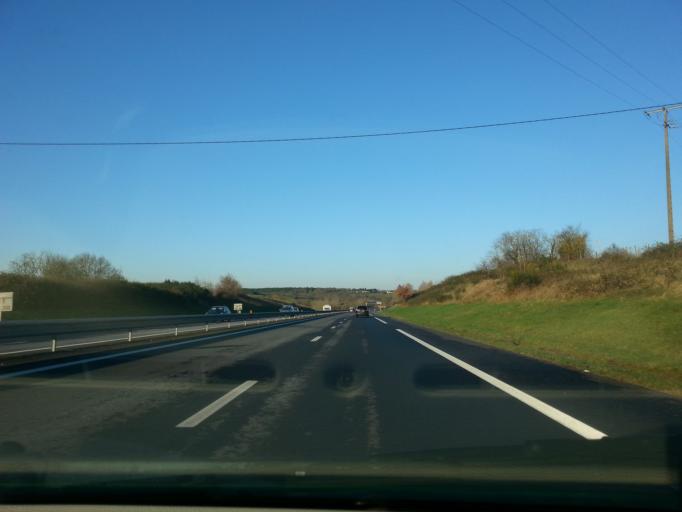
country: FR
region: Pays de la Loire
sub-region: Departement de Maine-et-Loire
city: Durtal
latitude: 47.6470
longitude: -0.2738
